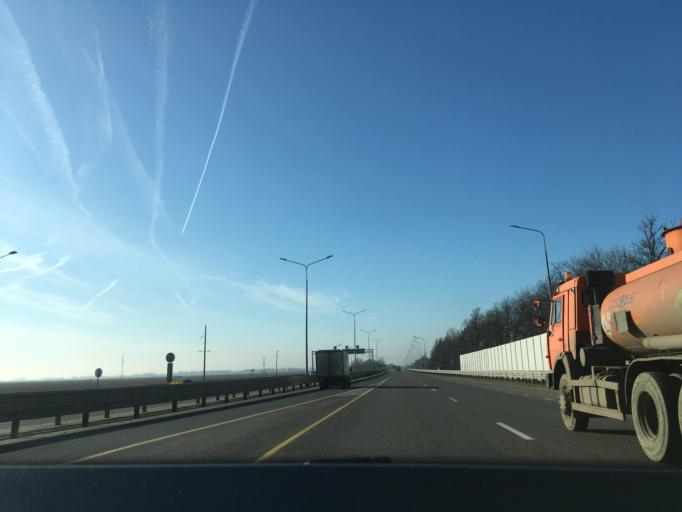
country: RU
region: Krasnodarskiy
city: Agronom
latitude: 45.1770
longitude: 39.1055
